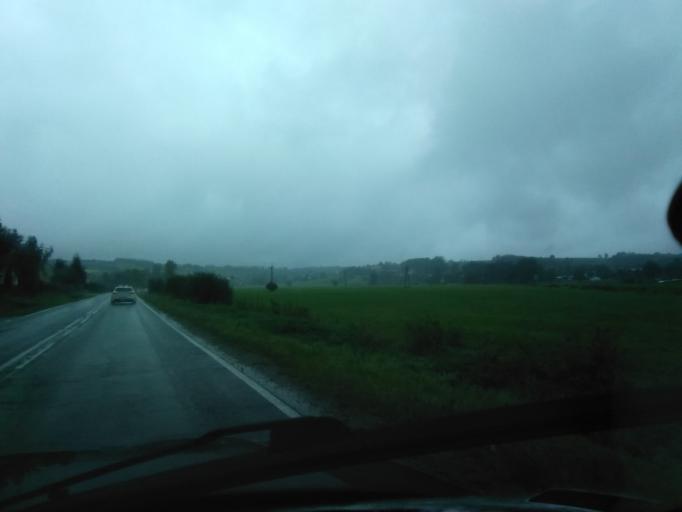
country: PL
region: Subcarpathian Voivodeship
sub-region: Powiat ropczycko-sedziszowski
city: Niedzwiada
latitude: 49.9760
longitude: 21.5651
